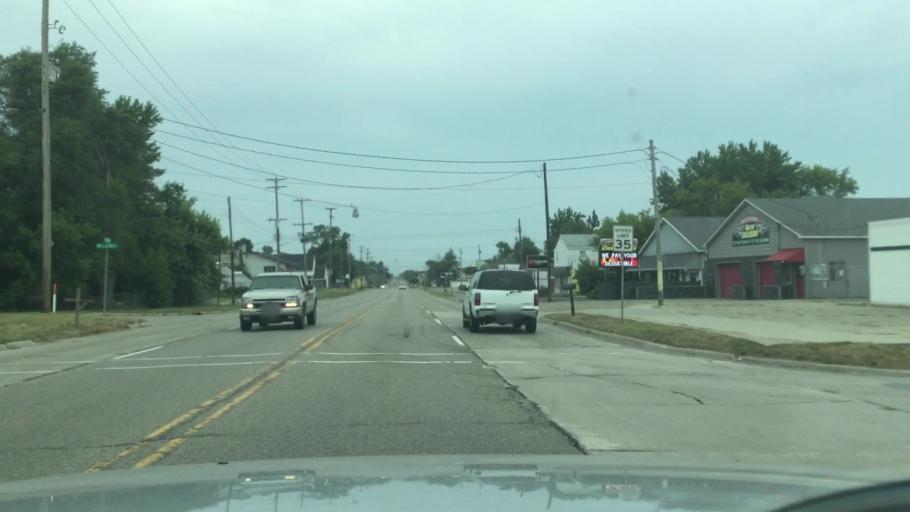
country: US
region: Michigan
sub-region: Genesee County
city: Flint
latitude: 42.9686
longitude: -83.6928
